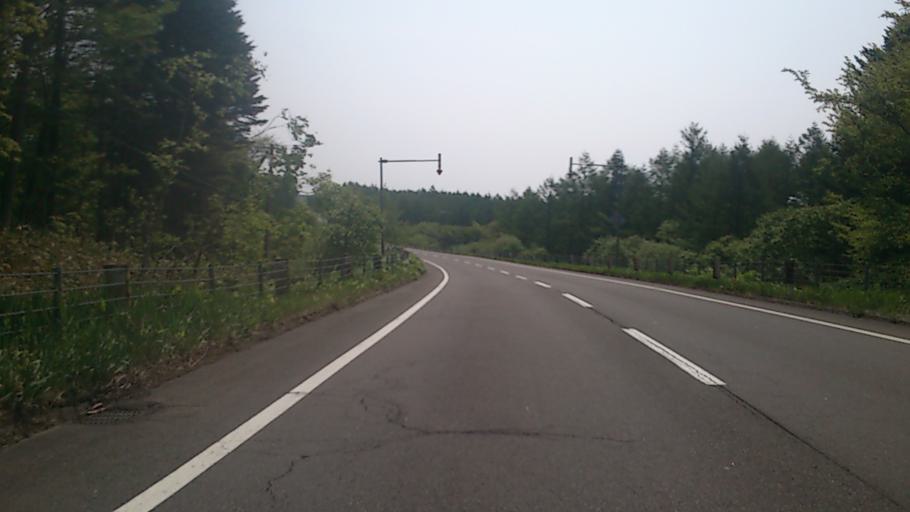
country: JP
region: Hokkaido
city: Kushiro
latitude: 43.4779
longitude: 144.5620
